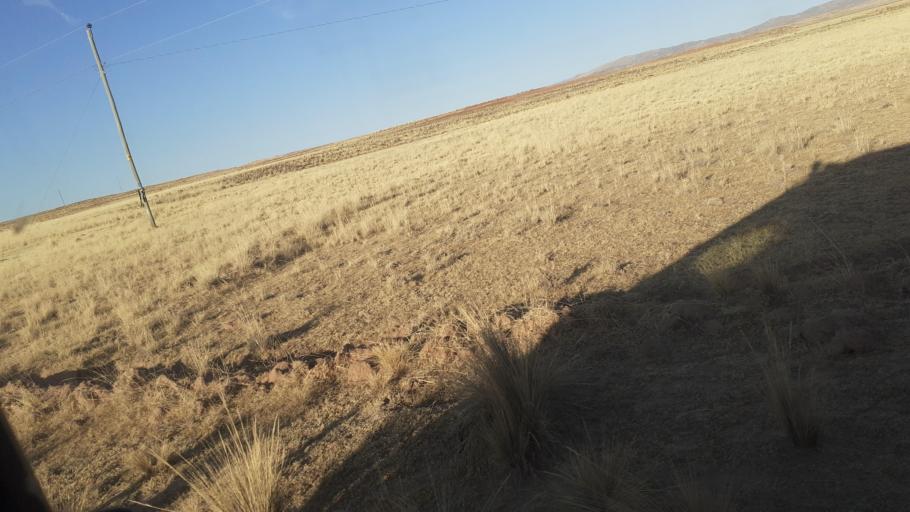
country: BO
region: La Paz
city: Tiahuanaco
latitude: -16.9544
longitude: -68.7582
